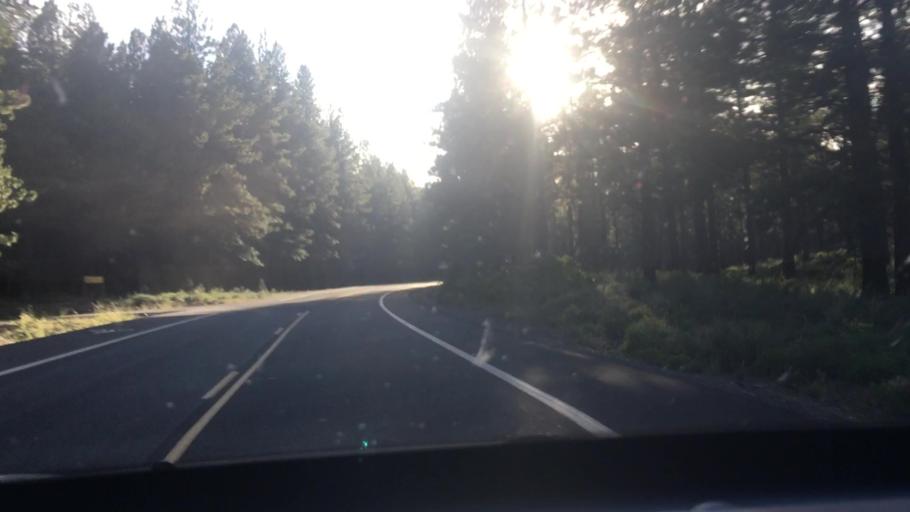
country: US
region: Oregon
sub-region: Deschutes County
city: Deschutes River Woods
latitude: 44.0360
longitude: -121.4561
